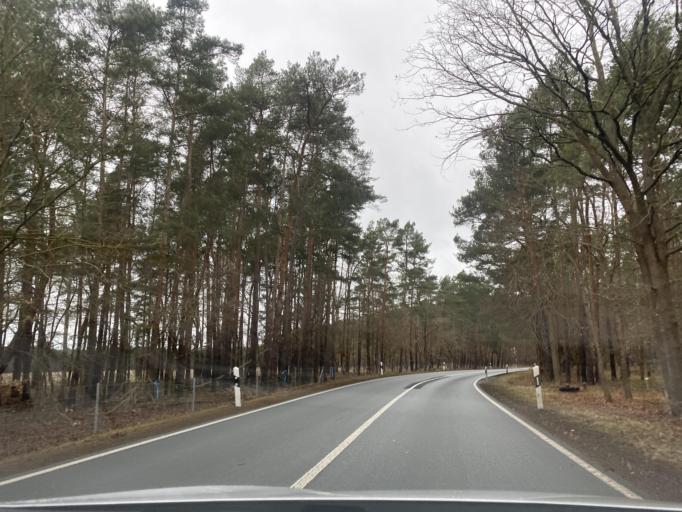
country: DE
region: Saxony
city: Rothenburg
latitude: 51.3892
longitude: 14.9537
